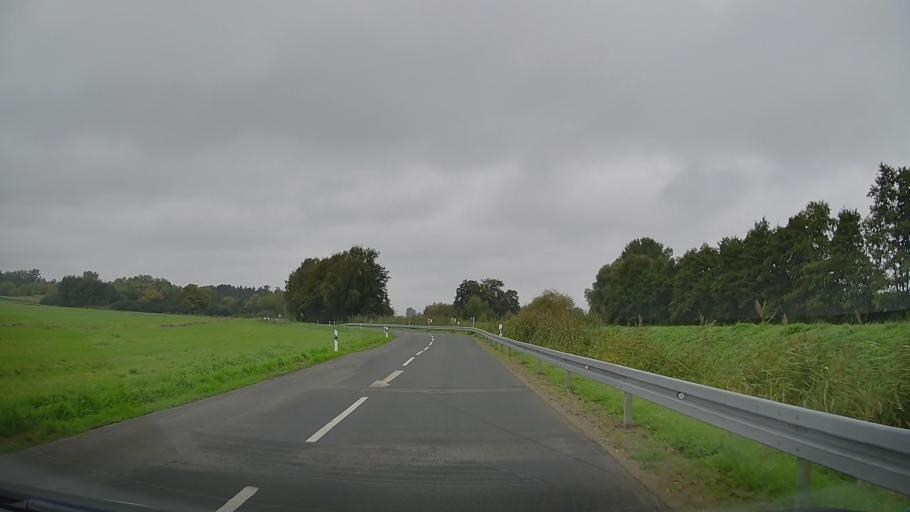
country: DE
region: Mecklenburg-Vorpommern
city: Guestrow
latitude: 53.8152
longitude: 12.1335
